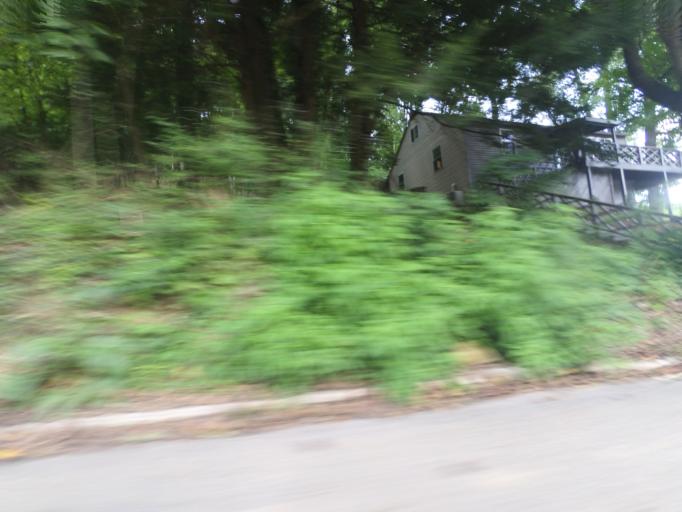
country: US
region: West Virginia
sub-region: Cabell County
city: Huntington
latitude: 38.3951
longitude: -82.4263
